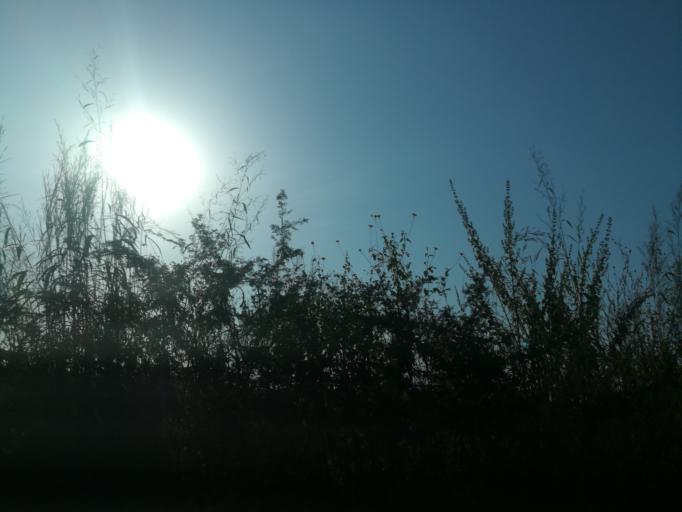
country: NG
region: Ogun
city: Abeokuta
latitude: 7.2333
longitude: 3.3009
